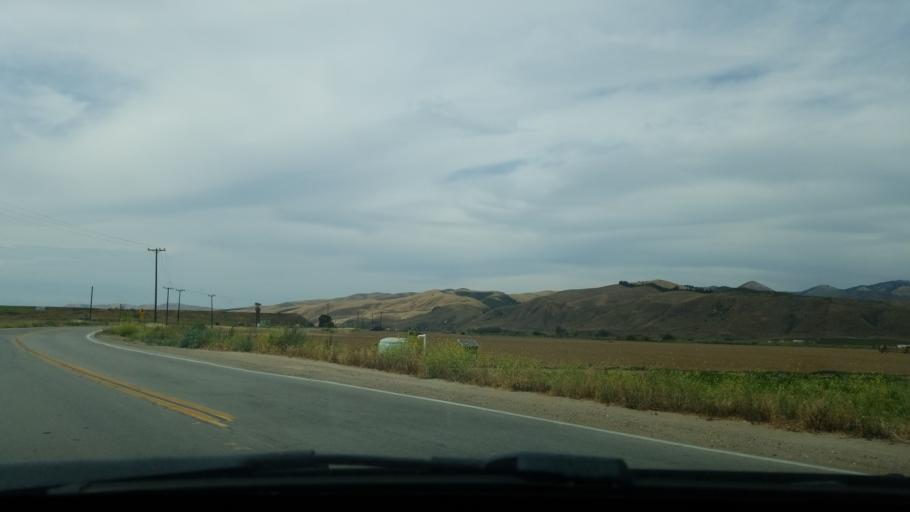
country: US
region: California
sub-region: Santa Barbara County
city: Orcutt
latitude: 34.8956
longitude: -120.3147
